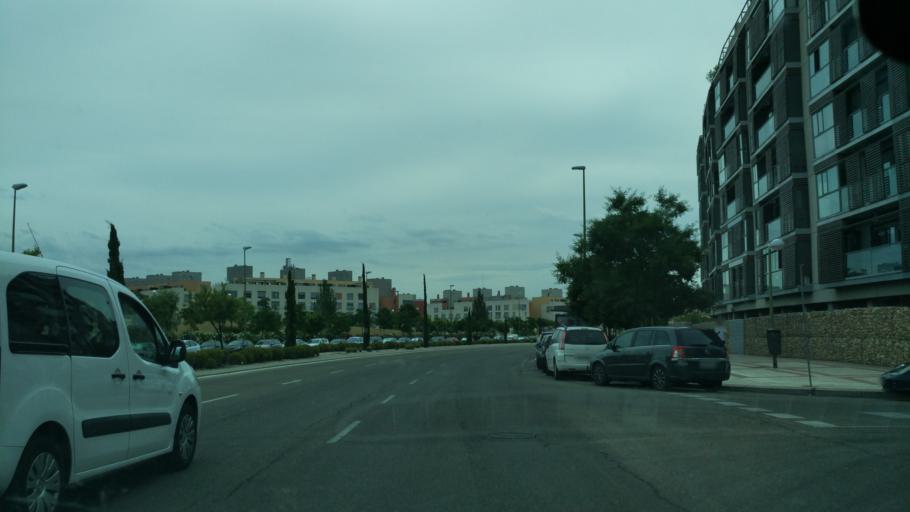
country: ES
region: Madrid
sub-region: Provincia de Madrid
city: Las Tablas
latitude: 40.5089
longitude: -3.6730
